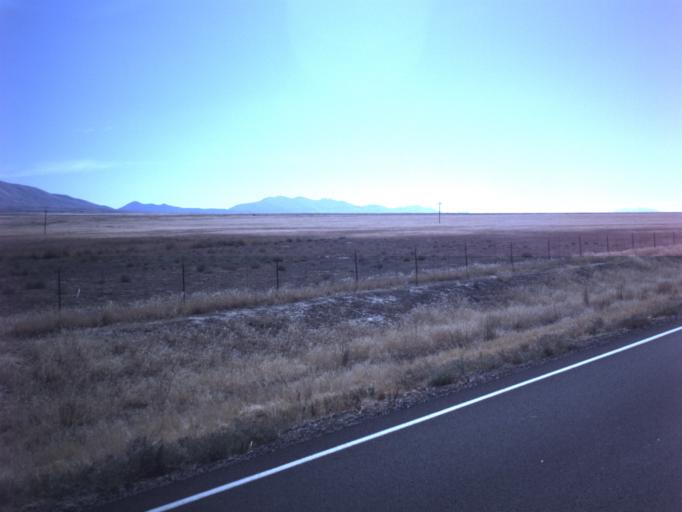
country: US
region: Utah
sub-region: Tooele County
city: Grantsville
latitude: 40.4402
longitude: -112.7487
